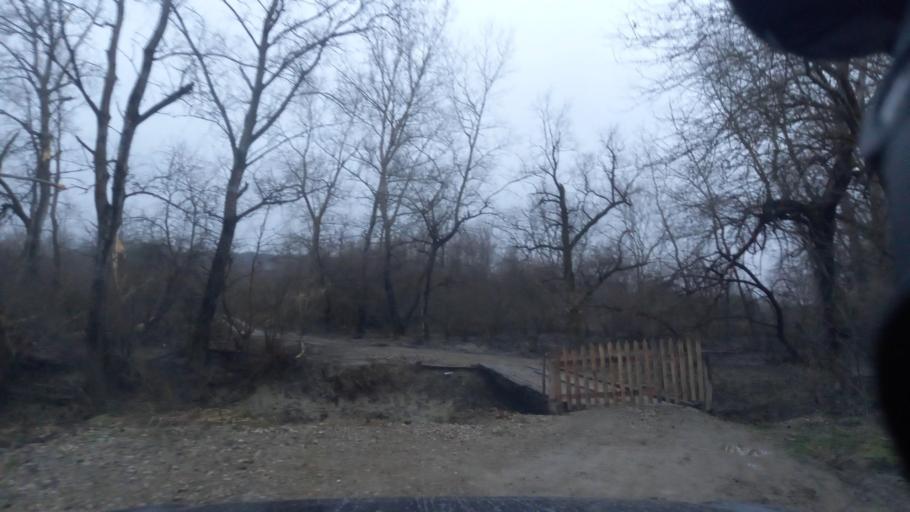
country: RU
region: Krasnodarskiy
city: Saratovskaya
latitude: 44.6457
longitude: 39.3163
